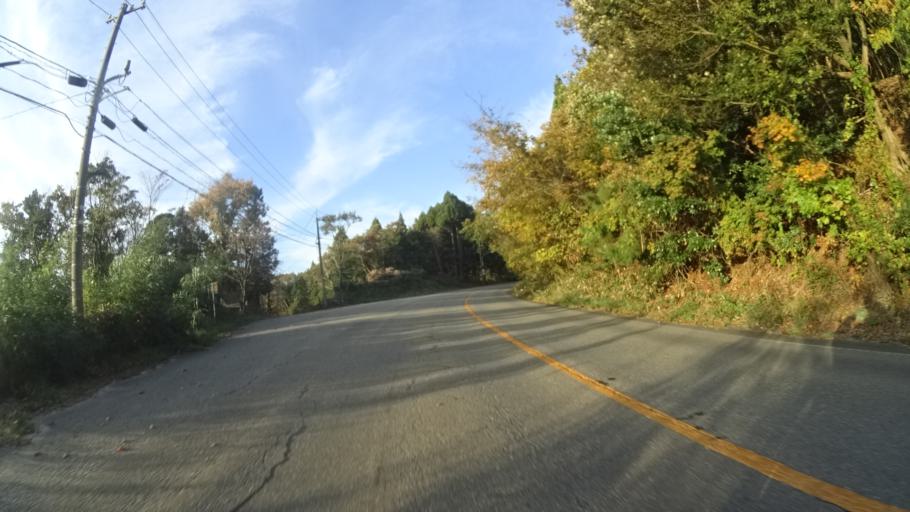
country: JP
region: Ishikawa
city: Nanao
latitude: 37.1659
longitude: 136.7138
